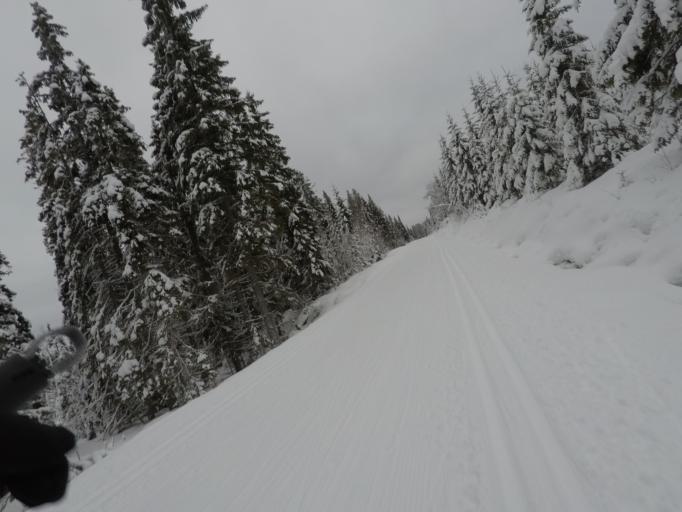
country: SE
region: Dalarna
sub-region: Ludvika Kommun
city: Abborrberget
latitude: 60.1460
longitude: 14.4830
